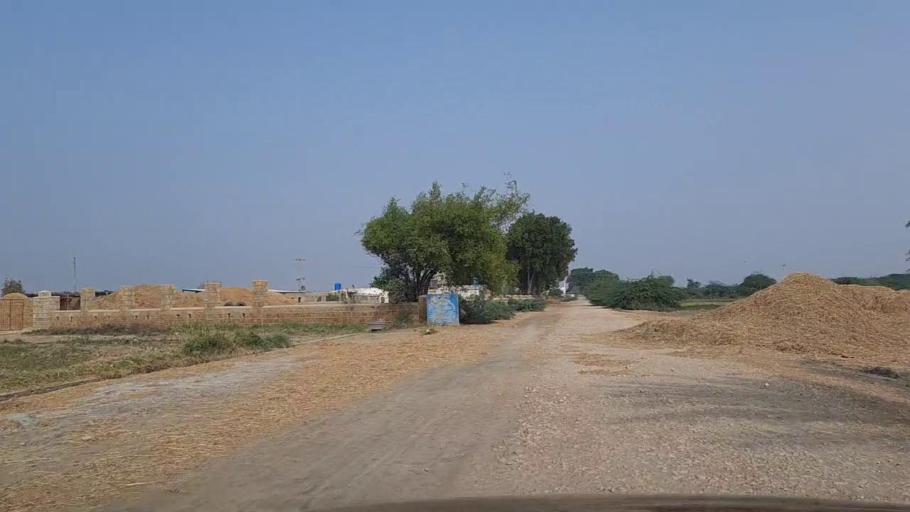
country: PK
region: Sindh
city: Thatta
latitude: 24.7662
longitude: 67.8710
